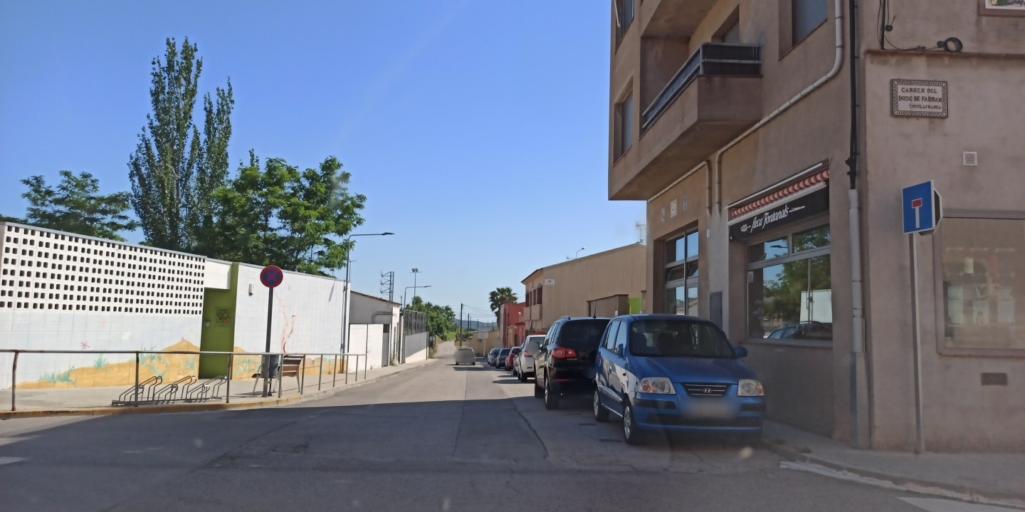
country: ES
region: Catalonia
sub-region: Provincia de Barcelona
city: La Granada
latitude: 41.3479
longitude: 1.7379
